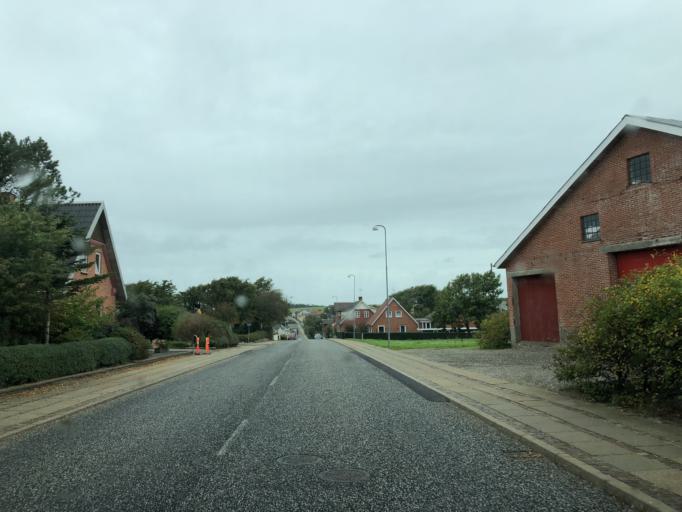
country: DK
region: North Denmark
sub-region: Thisted Kommune
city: Hurup
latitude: 56.7110
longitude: 8.4056
